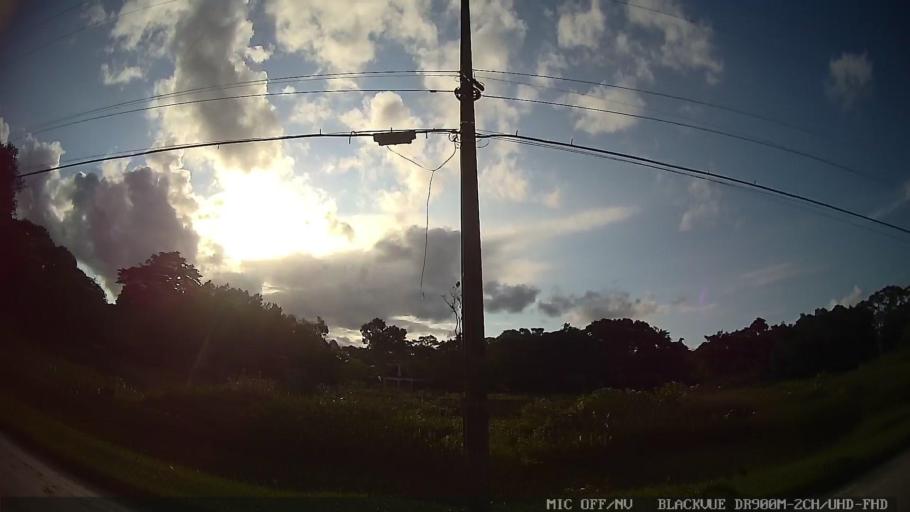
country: BR
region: Sao Paulo
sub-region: Itanhaem
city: Itanhaem
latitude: -24.1531
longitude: -46.8231
